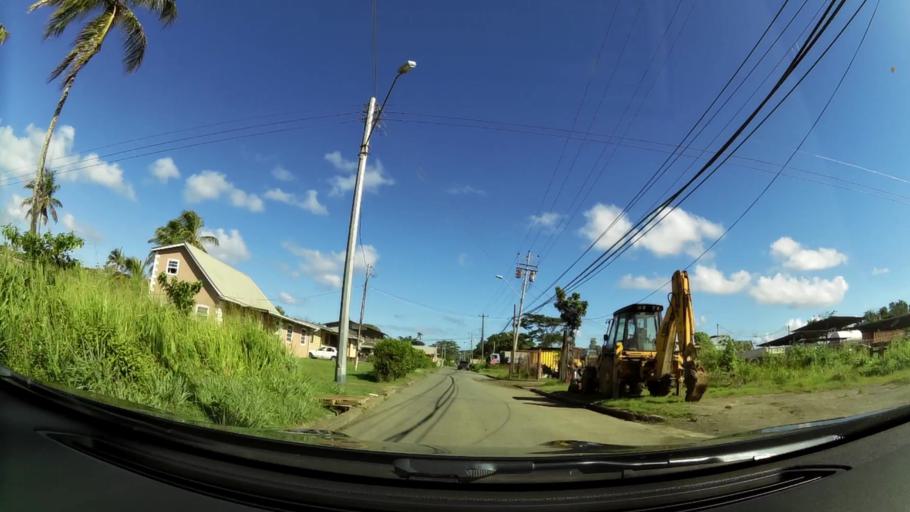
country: TT
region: Tobago
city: Scarborough
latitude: 11.1600
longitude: -60.7879
